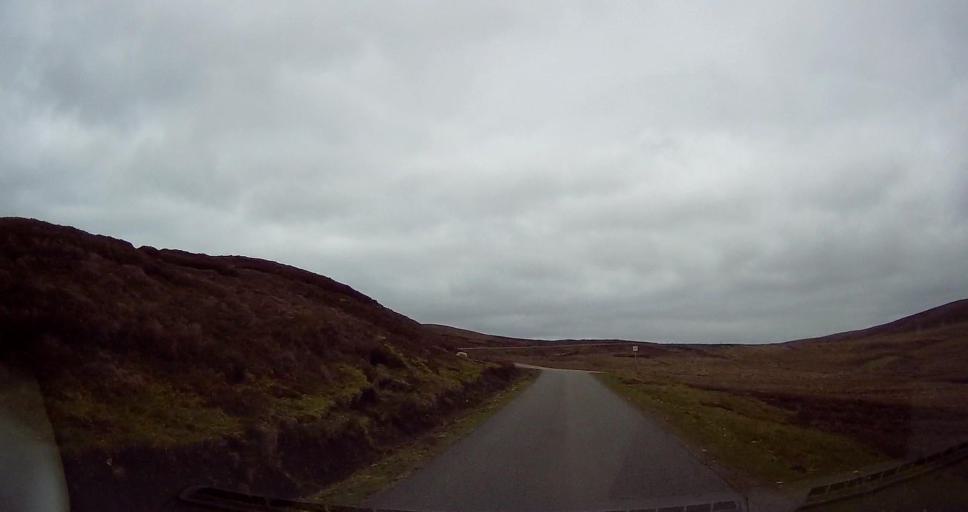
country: GB
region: Scotland
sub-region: Shetland Islands
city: Lerwick
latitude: 60.3165
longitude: -1.3419
